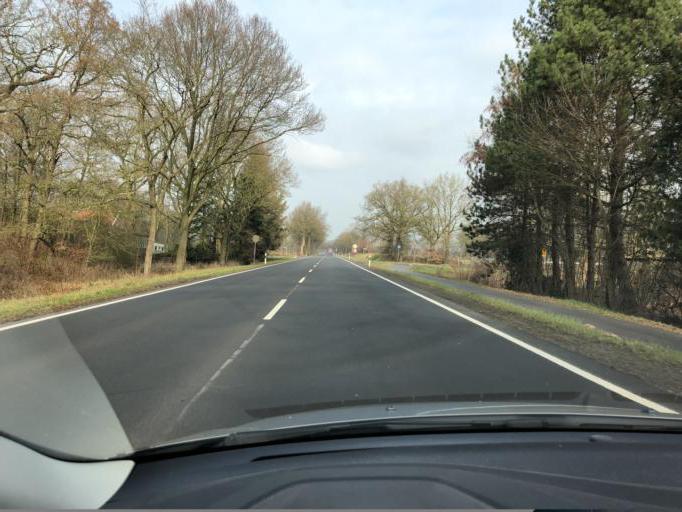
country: DE
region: Lower Saxony
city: Hesel
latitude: 53.3524
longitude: 7.6015
